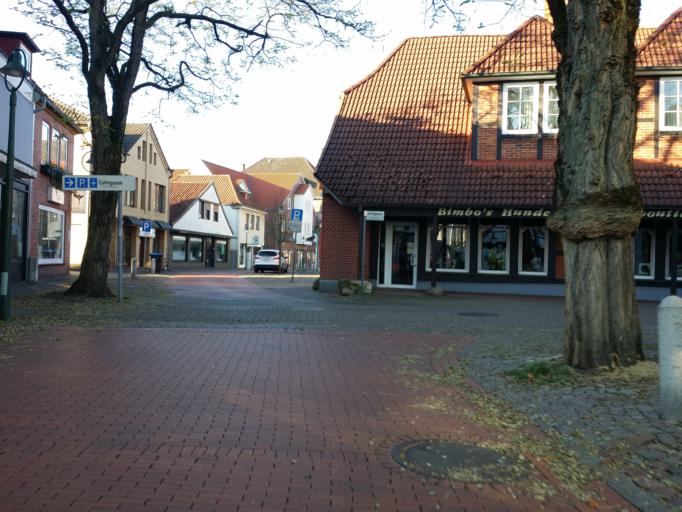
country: DE
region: Lower Saxony
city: Rotenburg
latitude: 53.1095
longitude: 9.4046
